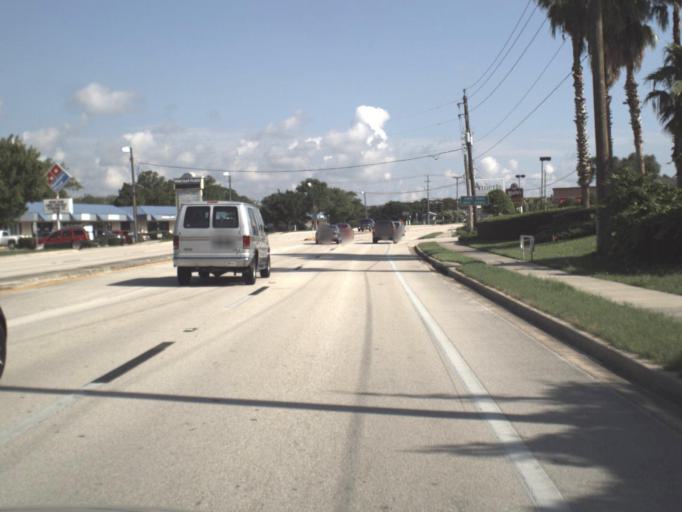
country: US
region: Florida
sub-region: Saint Johns County
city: Saint Augustine Beach
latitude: 29.8570
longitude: -81.2808
